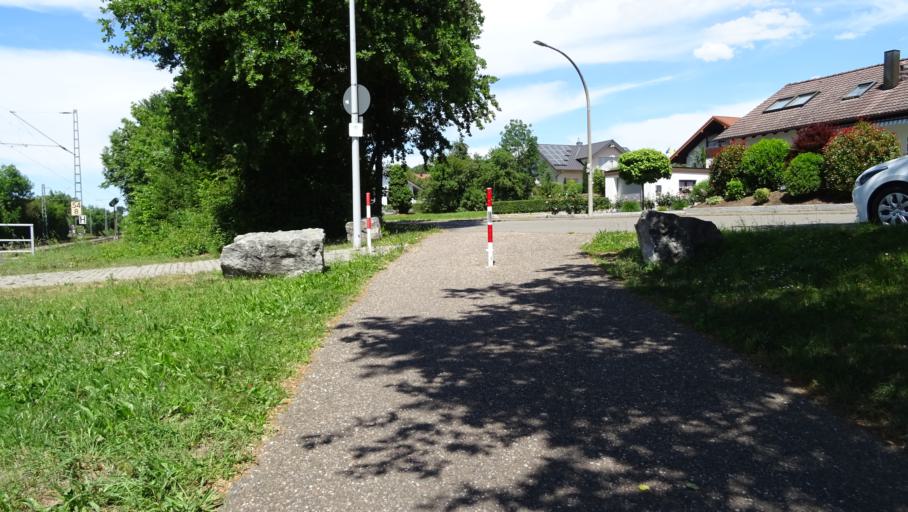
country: DE
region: Baden-Wuerttemberg
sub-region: Regierungsbezirk Stuttgart
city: Offenau
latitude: 49.2476
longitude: 9.1652
